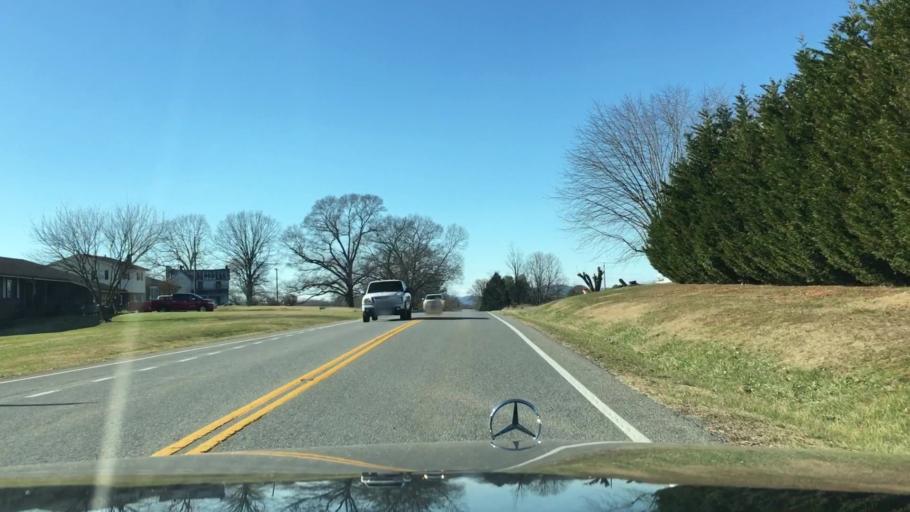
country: US
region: Virginia
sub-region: Botetourt County
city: Blue Ridge
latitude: 37.2526
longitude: -79.7046
